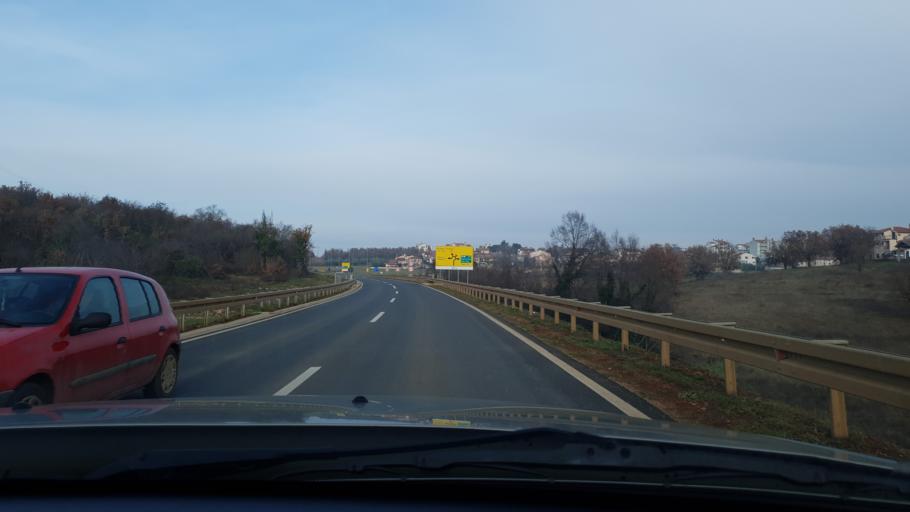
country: HR
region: Istarska
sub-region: Grad Porec
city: Porec
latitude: 45.2213
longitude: 13.6248
